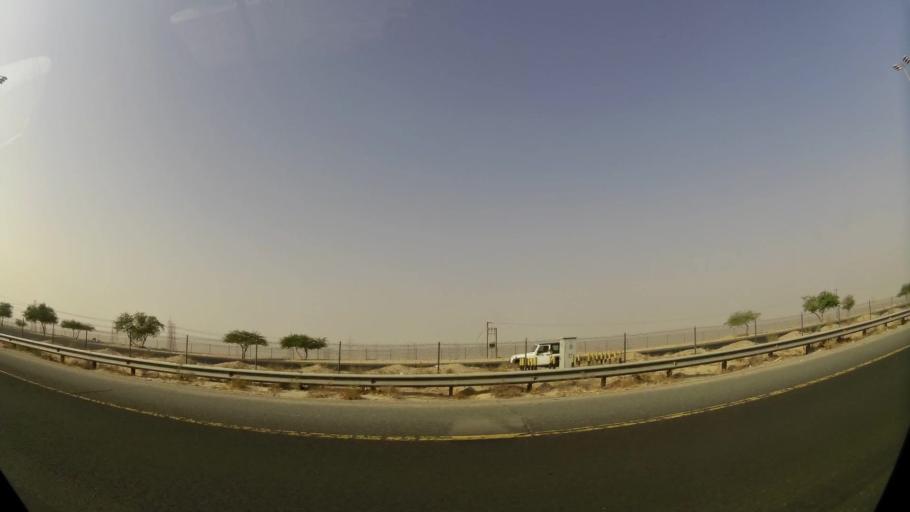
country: KW
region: Al Asimah
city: Ar Rabiyah
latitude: 29.1940
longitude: 47.8820
